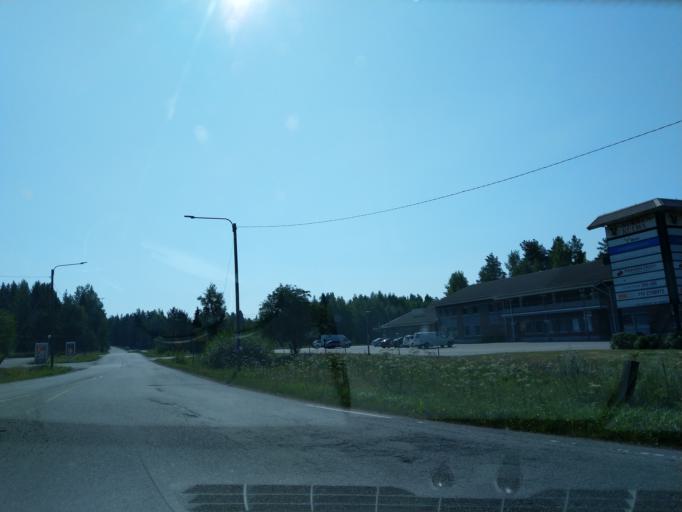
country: FI
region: Satakunta
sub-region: Pori
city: Noormarkku
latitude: 61.5845
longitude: 21.8510
